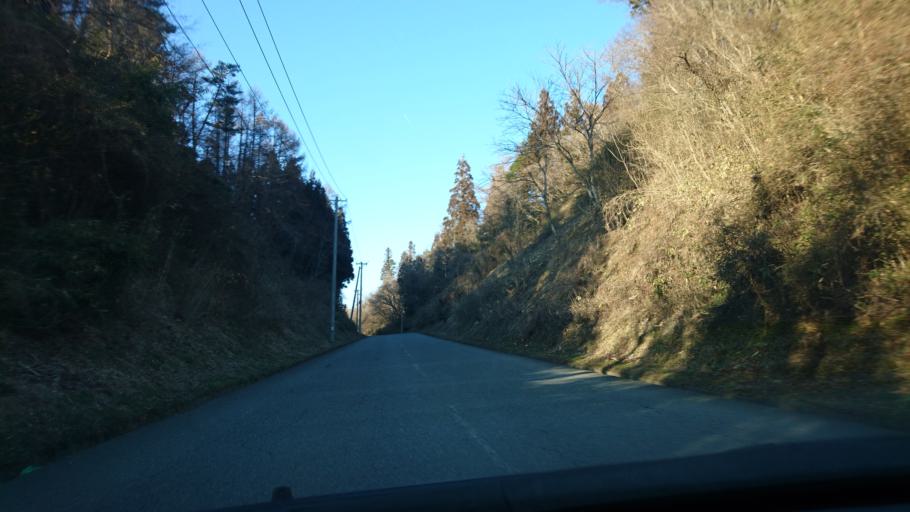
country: JP
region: Iwate
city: Ichinoseki
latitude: 38.9419
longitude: 141.3603
